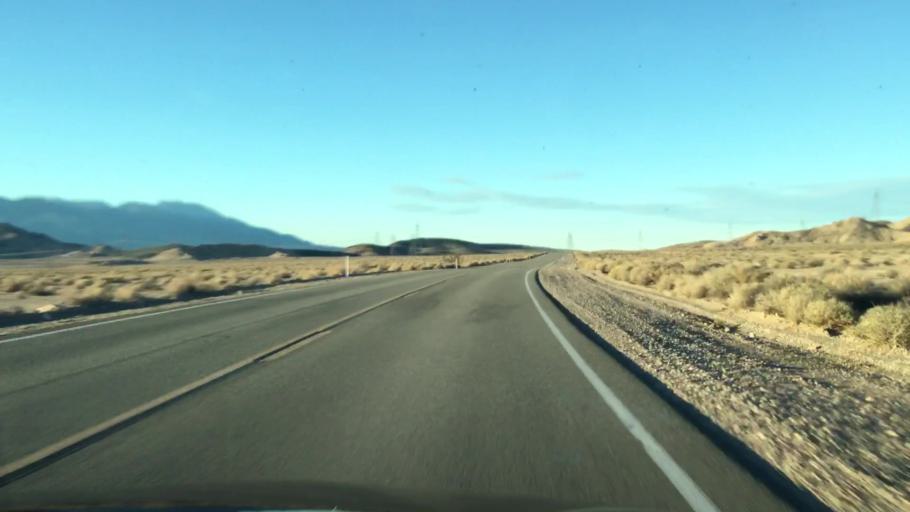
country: US
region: California
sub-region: San Bernardino County
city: Fort Irwin
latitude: 35.3758
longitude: -116.1212
